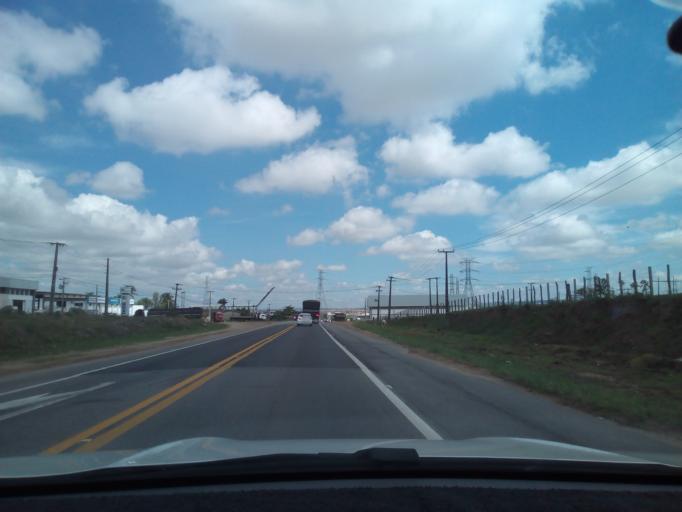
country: BR
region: Paraiba
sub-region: Campina Grande
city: Campina Grande
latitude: -7.2747
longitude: -35.9060
